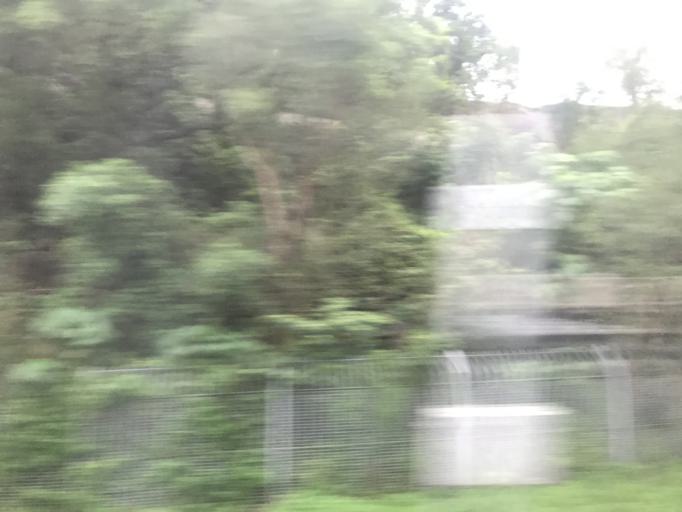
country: HK
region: Sha Tin
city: Sha Tin
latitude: 22.4107
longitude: 114.2106
